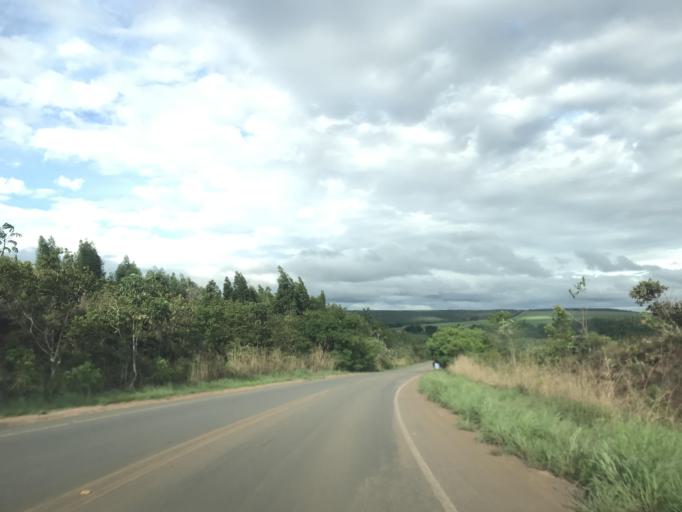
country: BR
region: Goias
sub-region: Vianopolis
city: Vianopolis
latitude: -16.5791
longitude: -48.3418
